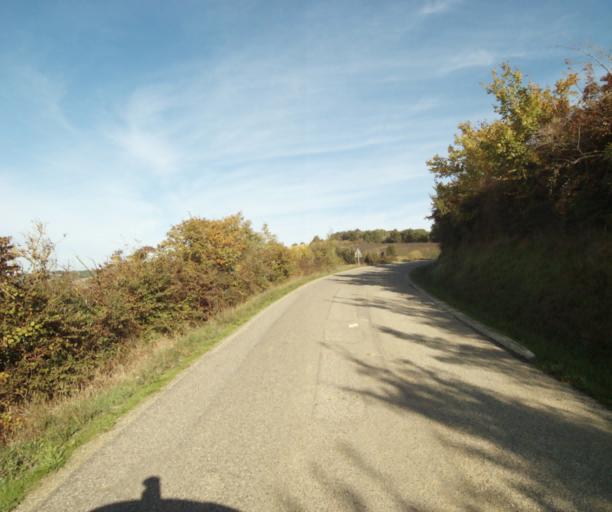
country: FR
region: Midi-Pyrenees
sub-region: Departement du Tarn-et-Garonne
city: Nohic
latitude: 43.9193
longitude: 1.4430
